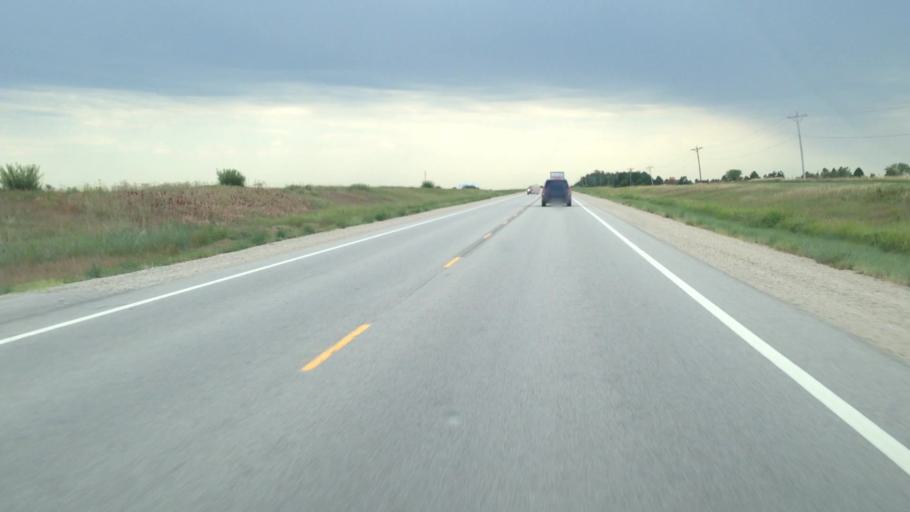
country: US
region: Kansas
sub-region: Coffey County
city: Burlington
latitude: 38.3217
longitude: -95.7291
